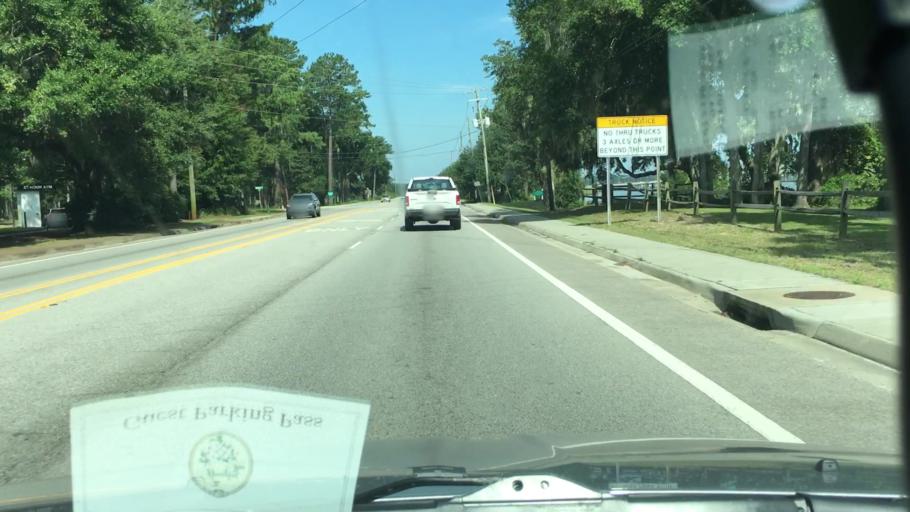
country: US
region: South Carolina
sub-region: Beaufort County
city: Beaufort
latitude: 32.4198
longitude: -80.6621
